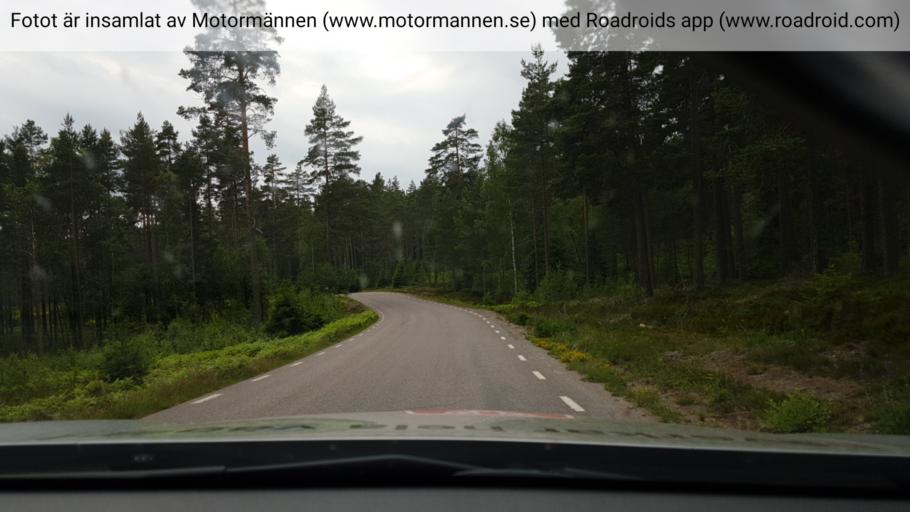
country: SE
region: Joenkoeping
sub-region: Habo Kommun
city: Habo
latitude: 58.0173
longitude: 14.0058
